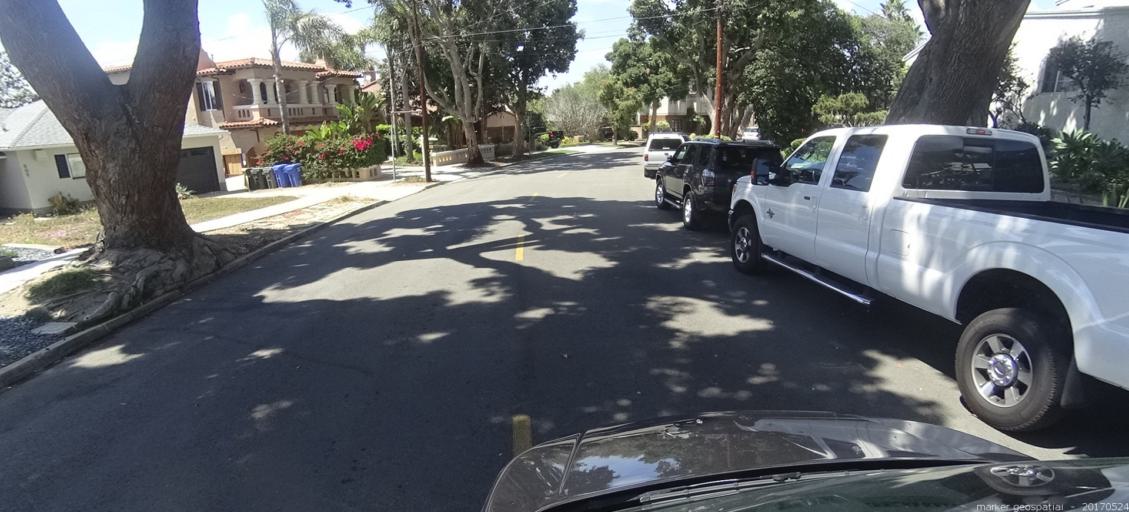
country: US
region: California
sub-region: Los Angeles County
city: Redondo Beach
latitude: 33.8307
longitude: -118.3840
